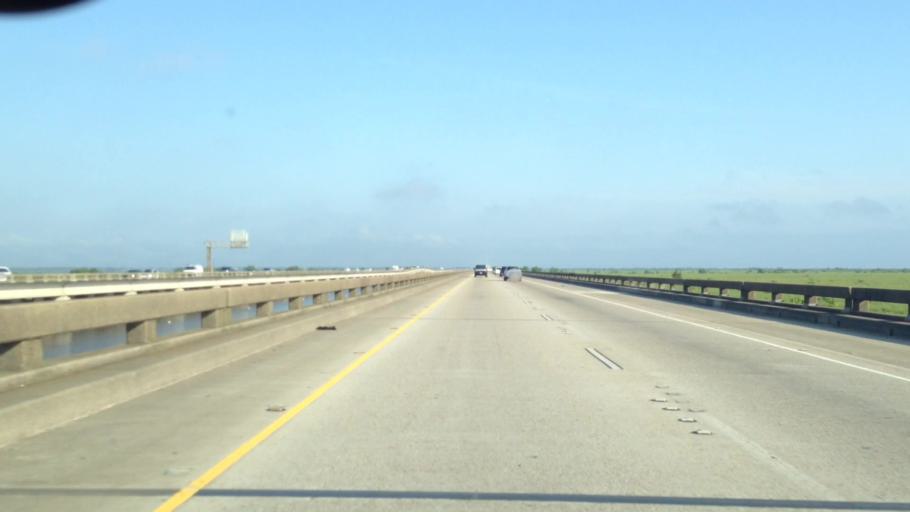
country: US
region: Louisiana
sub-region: Saint Charles Parish
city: Ama
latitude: 30.0231
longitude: -90.3235
